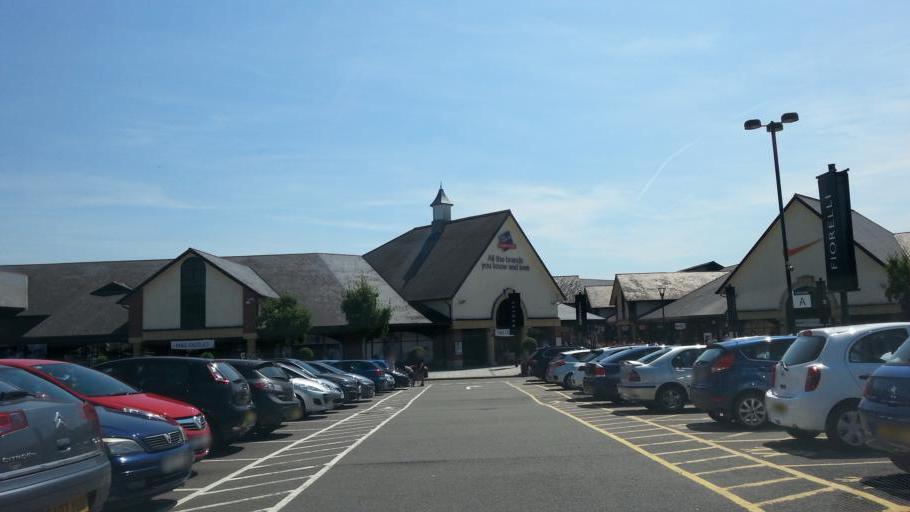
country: GB
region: England
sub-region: Derbyshire
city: Pinxton
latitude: 53.1075
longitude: -1.3127
